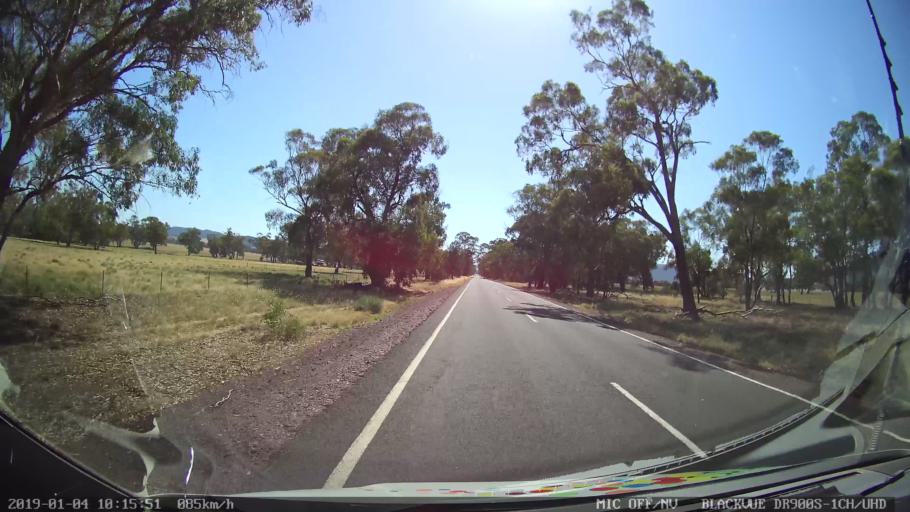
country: AU
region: New South Wales
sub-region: Cabonne
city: Canowindra
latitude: -33.3864
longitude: 148.4277
